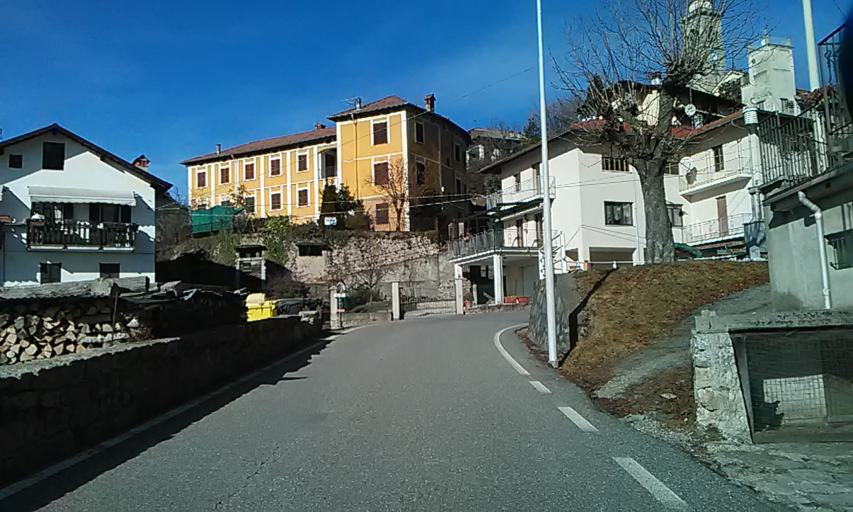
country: IT
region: Piedmont
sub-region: Provincia di Vercelli
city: Cellio
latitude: 45.7526
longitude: 8.3118
